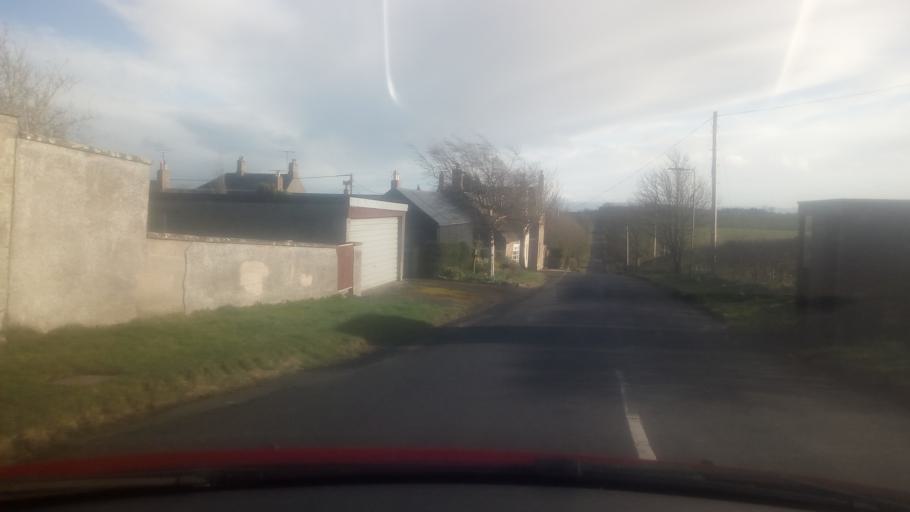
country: GB
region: Scotland
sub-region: The Scottish Borders
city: Duns
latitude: 55.7620
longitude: -2.3726
